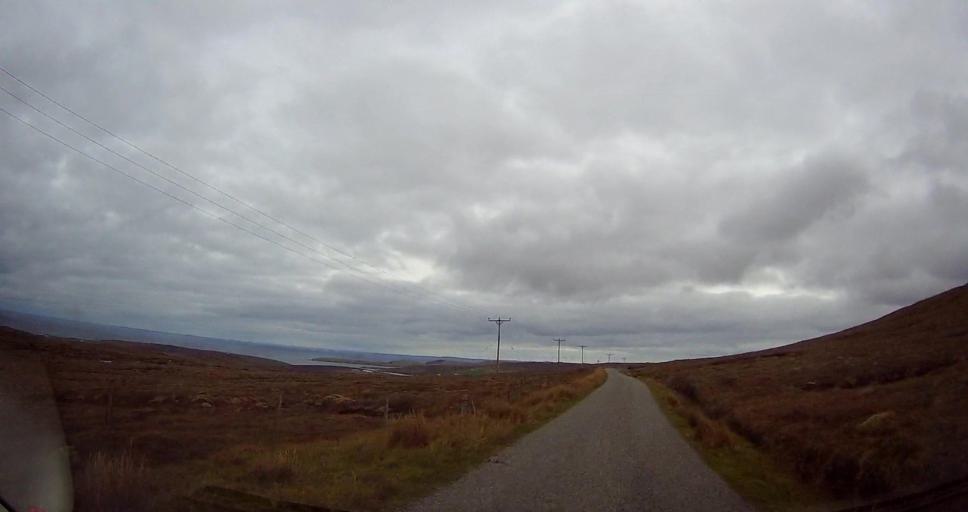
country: GB
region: Scotland
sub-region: Shetland Islands
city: Shetland
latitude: 60.5734
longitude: -1.0664
